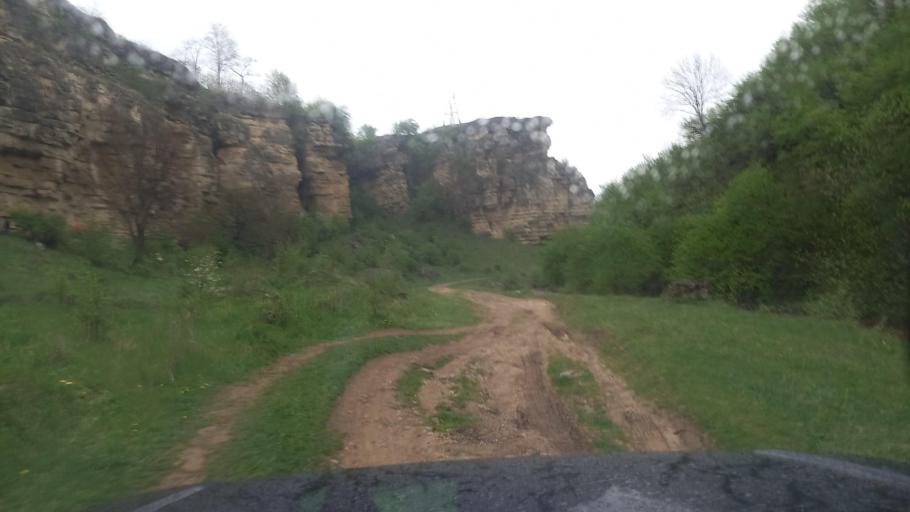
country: RU
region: Stavropol'skiy
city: Kislovodsk
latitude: 43.8851
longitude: 42.6990
